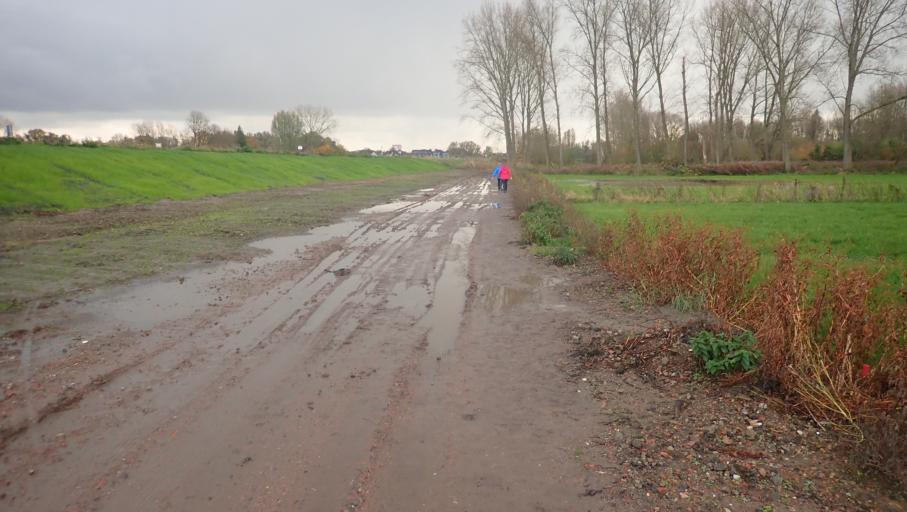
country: BE
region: Flanders
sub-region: Provincie Oost-Vlaanderen
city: Hamme
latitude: 51.1072
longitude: 4.1281
